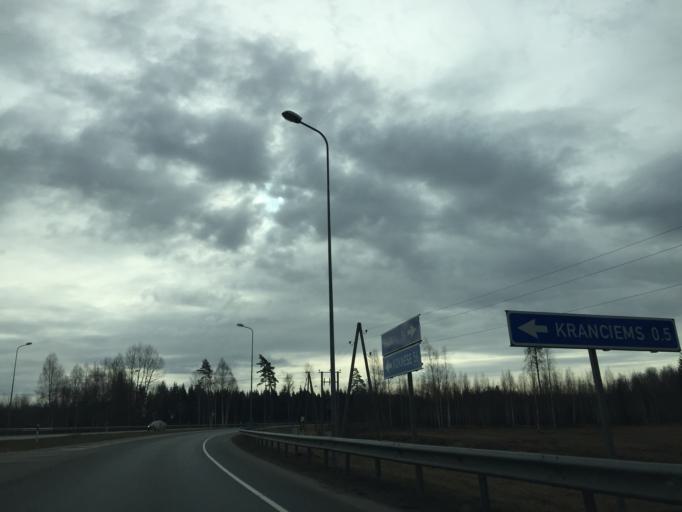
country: LV
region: Ogre
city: Ogre
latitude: 56.8584
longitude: 24.6415
